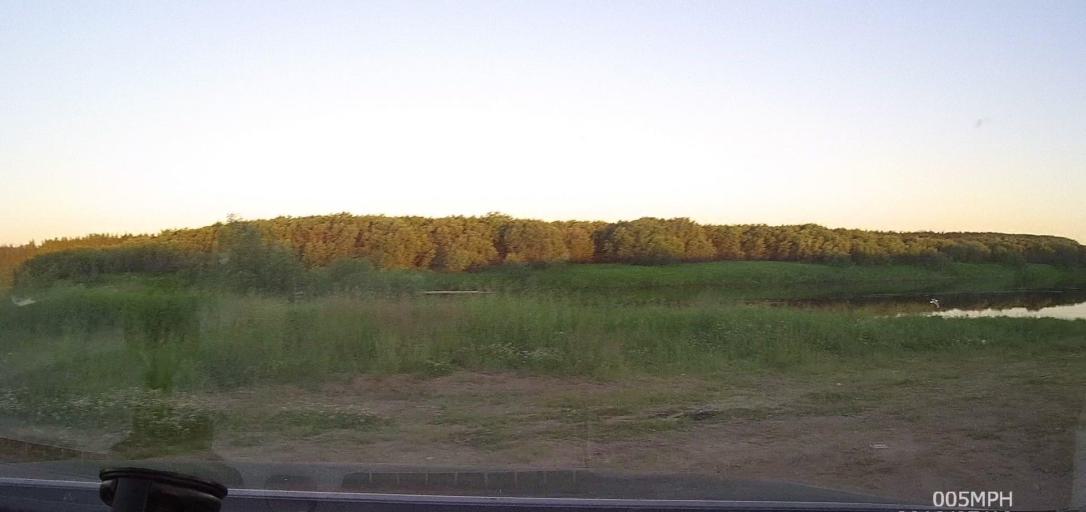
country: RU
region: Arkhangelskaya
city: Lukovetskiy
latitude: 64.2346
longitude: 42.7130
